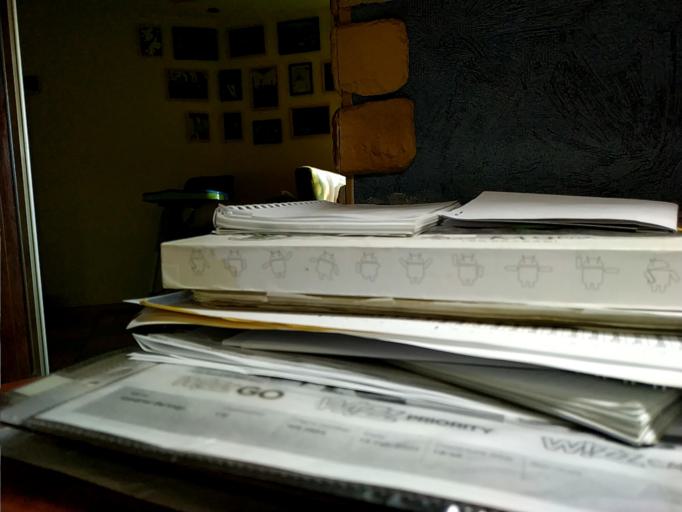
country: RU
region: Novgorod
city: Kholm
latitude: 57.1137
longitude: 31.4837
